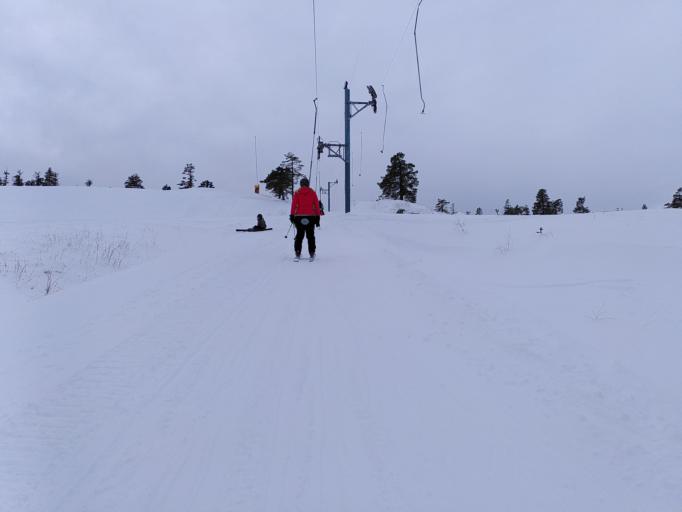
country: NO
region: Buskerud
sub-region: Flesberg
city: Lampeland
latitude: 59.8026
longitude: 9.3948
